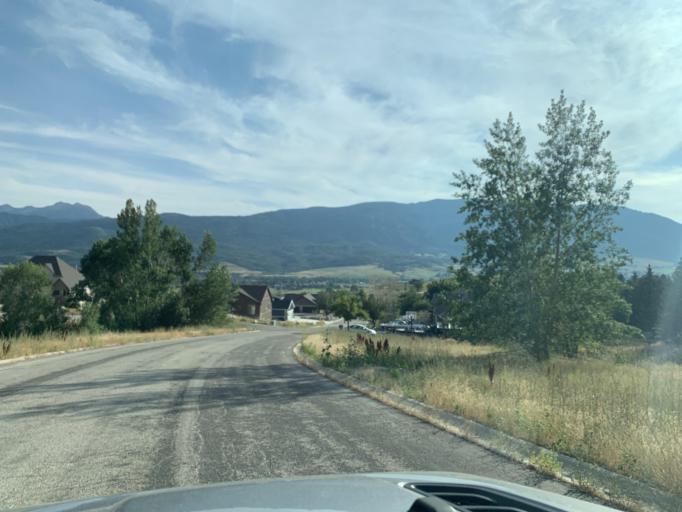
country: US
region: Utah
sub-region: Weber County
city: Wolf Creek
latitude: 41.3243
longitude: -111.8155
